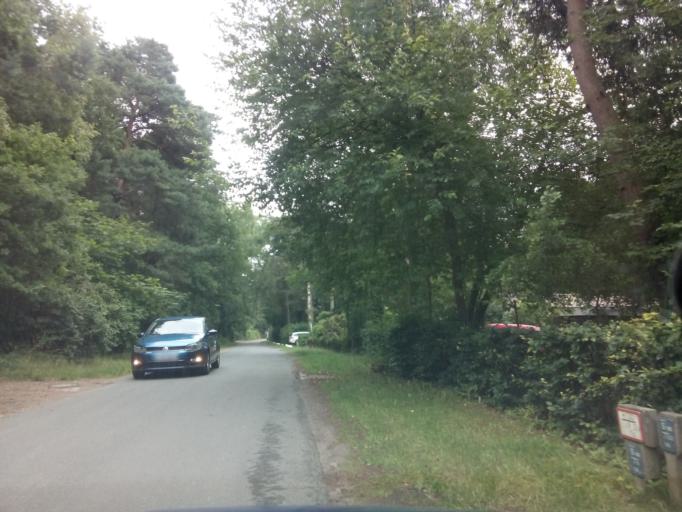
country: DE
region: Lower Saxony
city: Worpswede
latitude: 53.2099
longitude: 8.9191
